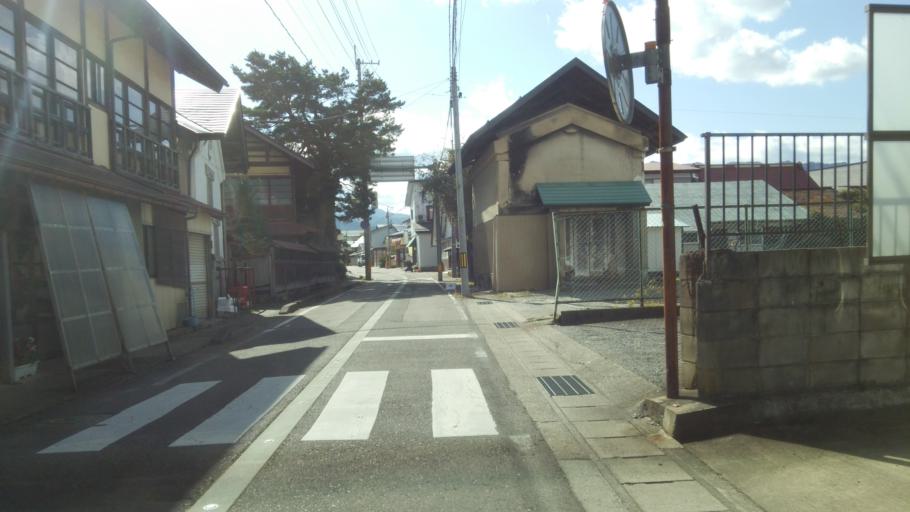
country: JP
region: Fukushima
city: Kitakata
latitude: 37.4478
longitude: 139.8305
